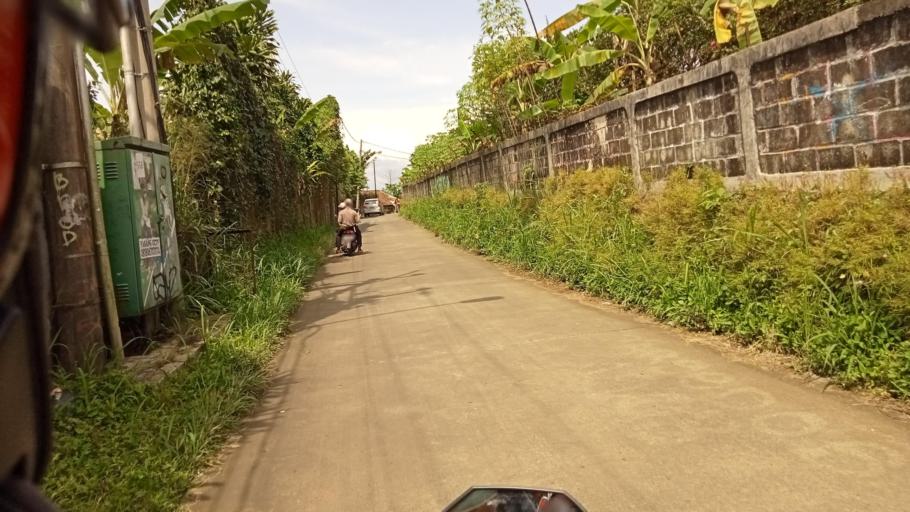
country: ID
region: West Java
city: Caringin
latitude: -6.6448
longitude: 106.9036
